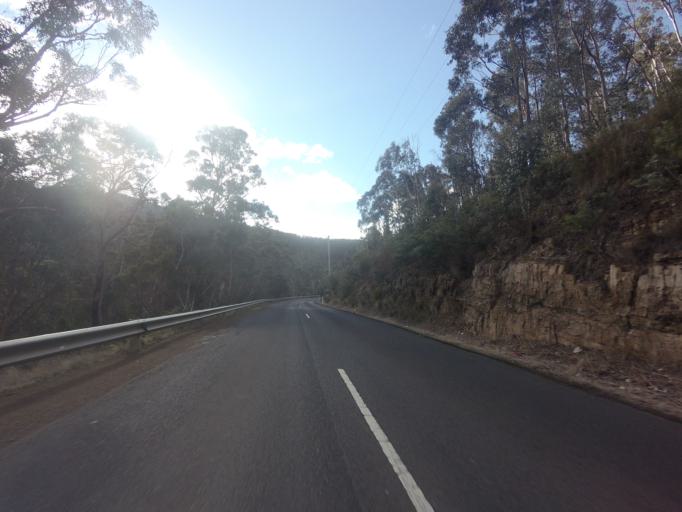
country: AU
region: Tasmania
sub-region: Glenorchy
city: Berriedale
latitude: -42.8235
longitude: 147.2102
